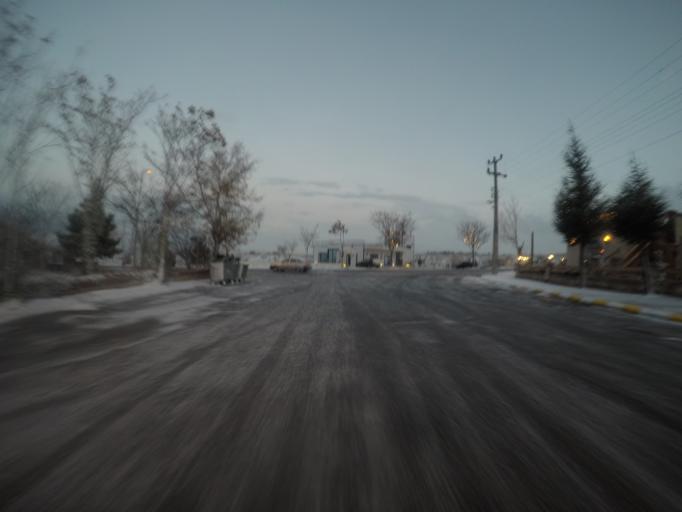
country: TR
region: Nevsehir
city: Goereme
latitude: 38.6216
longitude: 34.8040
